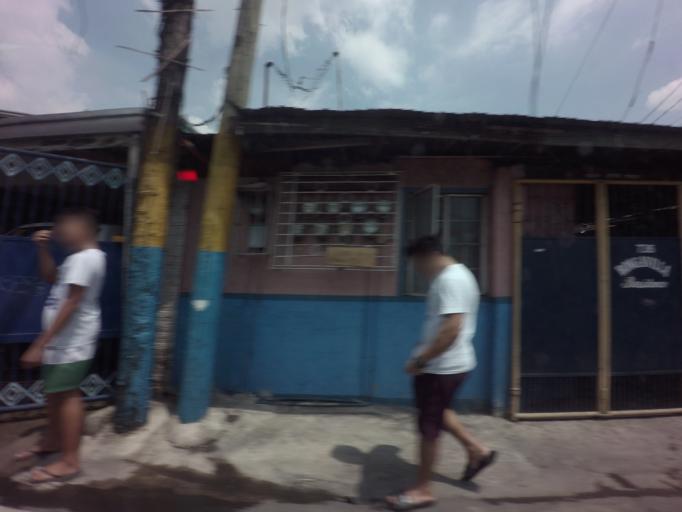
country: PH
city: Sambayanihan People's Village
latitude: 14.4611
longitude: 121.0543
